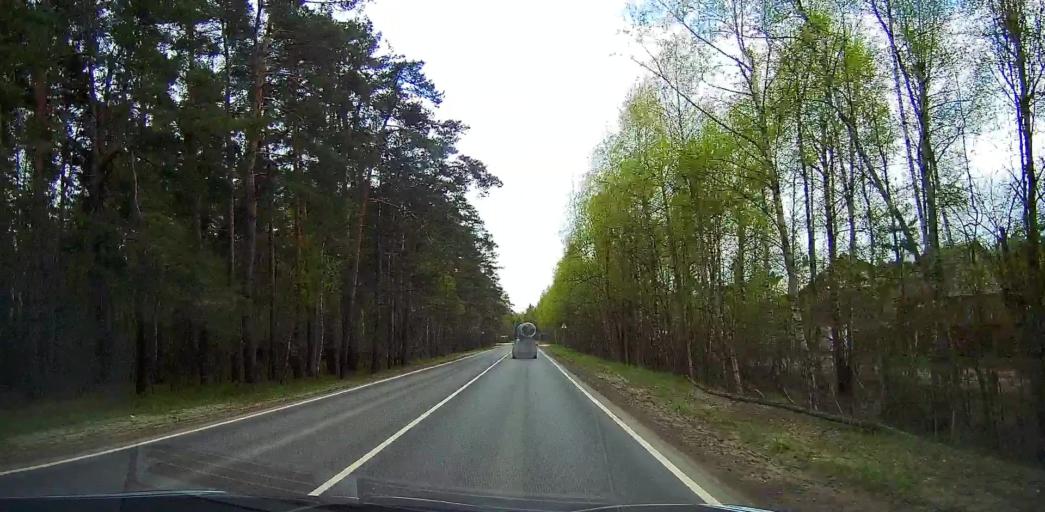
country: RU
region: Moskovskaya
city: Beloozerskiy
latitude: 55.4941
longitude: 38.4286
